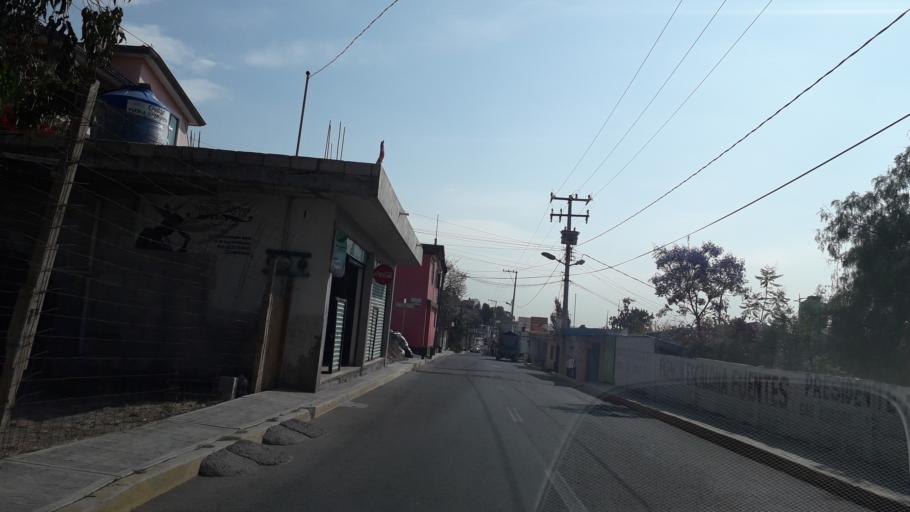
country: MX
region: Puebla
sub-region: Puebla
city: San Andres Azumiatla
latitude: 18.9031
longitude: -98.2554
